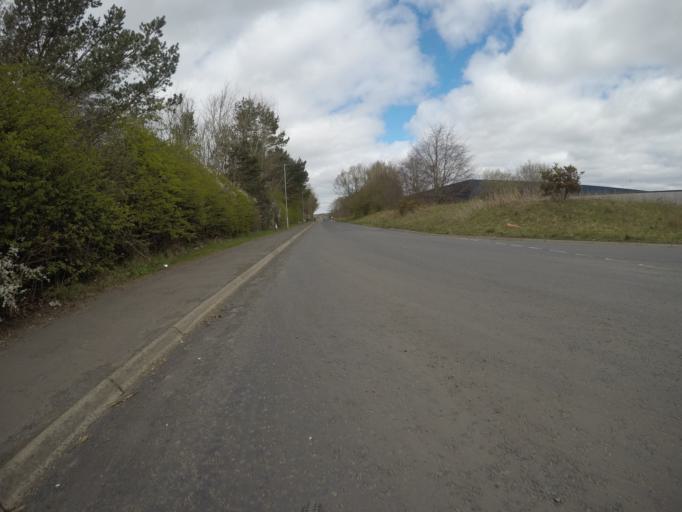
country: GB
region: Scotland
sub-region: North Ayrshire
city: Irvine
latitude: 55.6163
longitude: -4.6449
